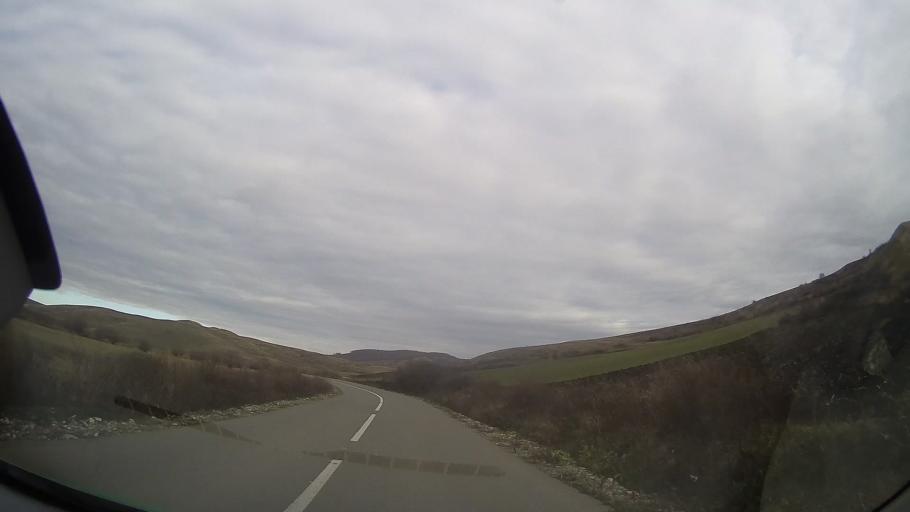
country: RO
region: Bistrita-Nasaud
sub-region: Comuna Silvasu de Campie
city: Silvasu de Campie
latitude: 46.8003
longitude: 24.2971
